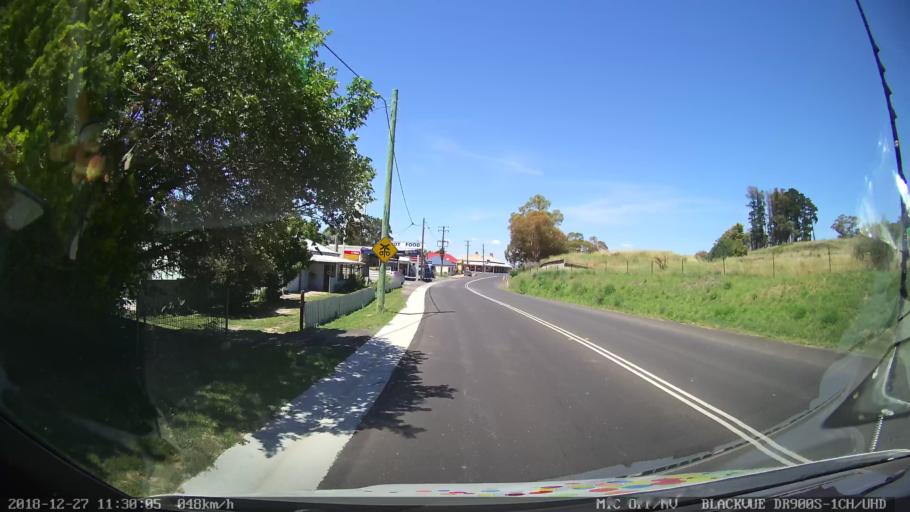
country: AU
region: New South Wales
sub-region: Bathurst Regional
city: Perthville
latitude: -33.4853
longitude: 149.5476
